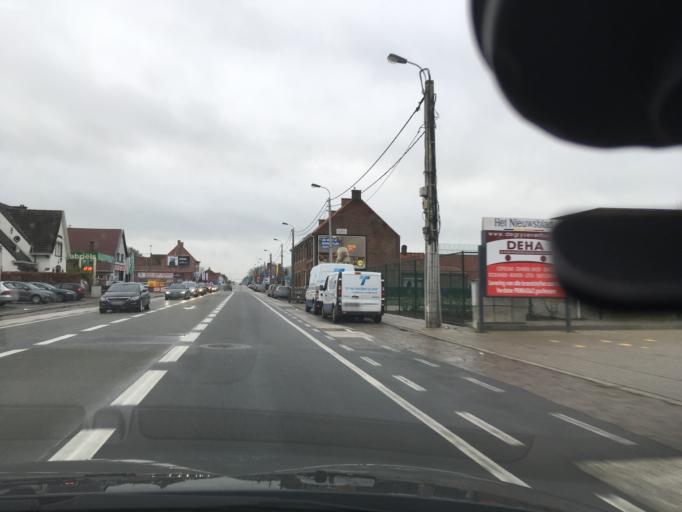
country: BE
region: Flanders
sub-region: Provincie West-Vlaanderen
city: Roeselare
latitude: 50.9334
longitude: 3.1203
